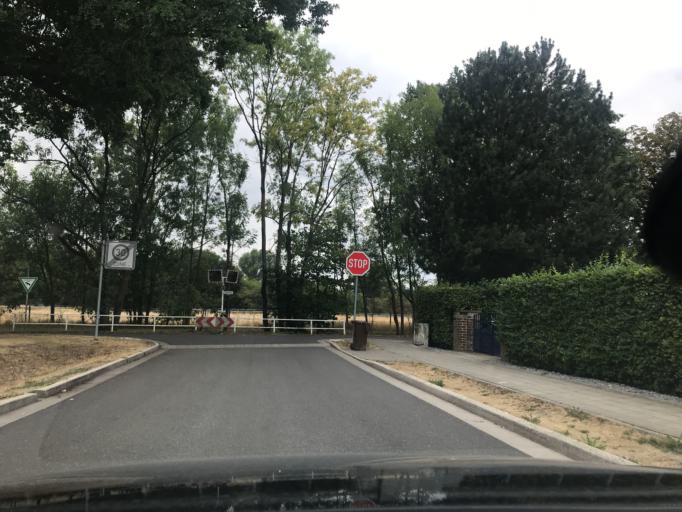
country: DE
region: North Rhine-Westphalia
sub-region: Regierungsbezirk Dusseldorf
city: Krefeld
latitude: 51.3570
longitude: 6.5619
